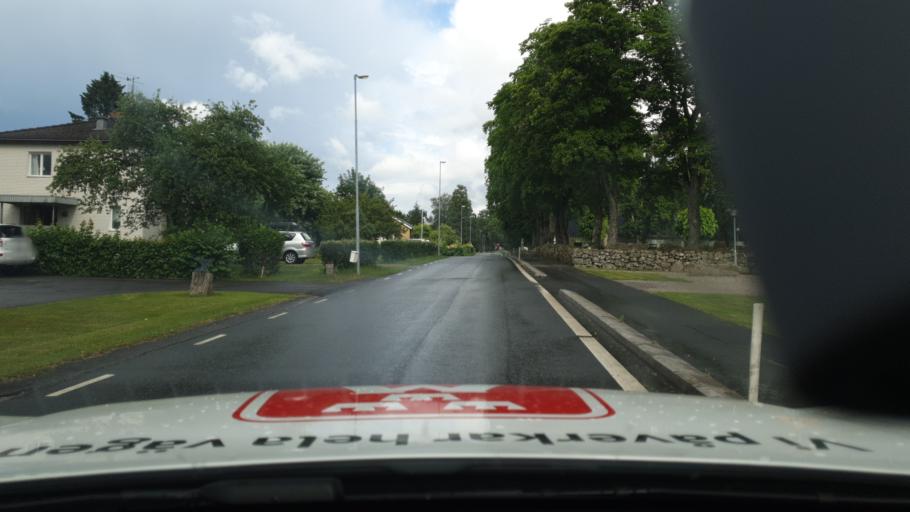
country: SE
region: Vaestra Goetaland
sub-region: Falkopings Kommun
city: Falkoeping
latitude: 58.0220
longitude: 13.5710
